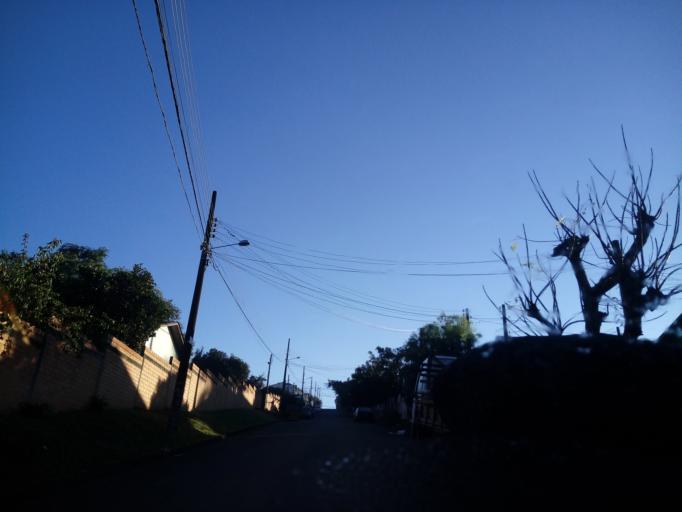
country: BR
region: Santa Catarina
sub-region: Chapeco
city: Chapeco
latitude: -27.1248
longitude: -52.6219
